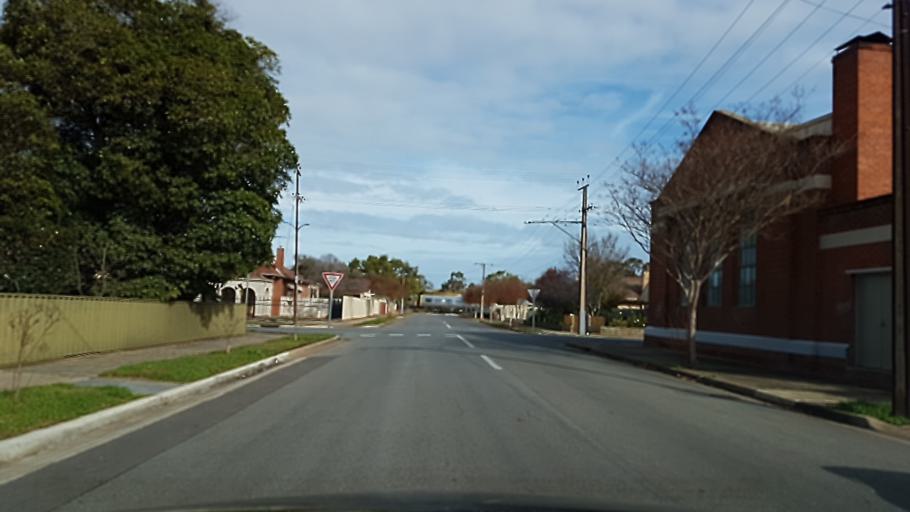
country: AU
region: South Australia
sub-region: Charles Sturt
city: Woodville North
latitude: -34.8785
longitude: 138.5422
